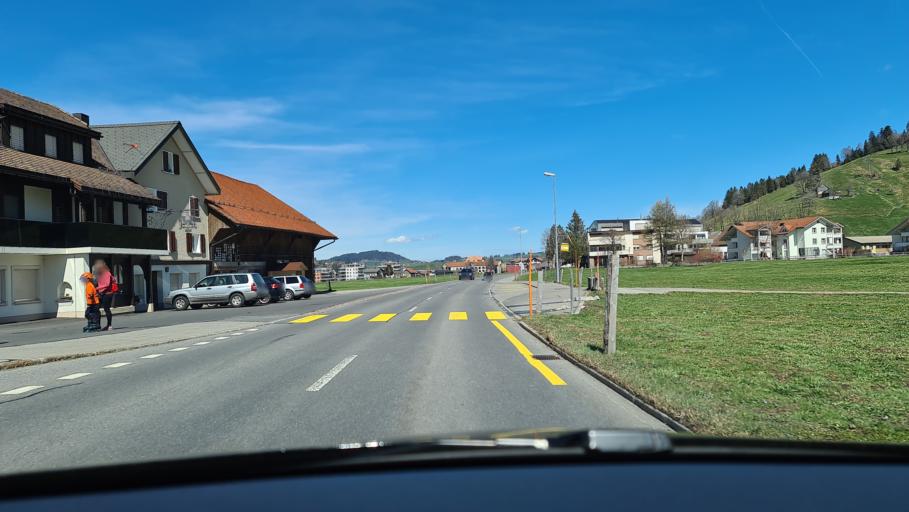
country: CH
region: Schwyz
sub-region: Bezirk Einsiedeln
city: Einsiedeln
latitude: 47.1160
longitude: 8.7371
